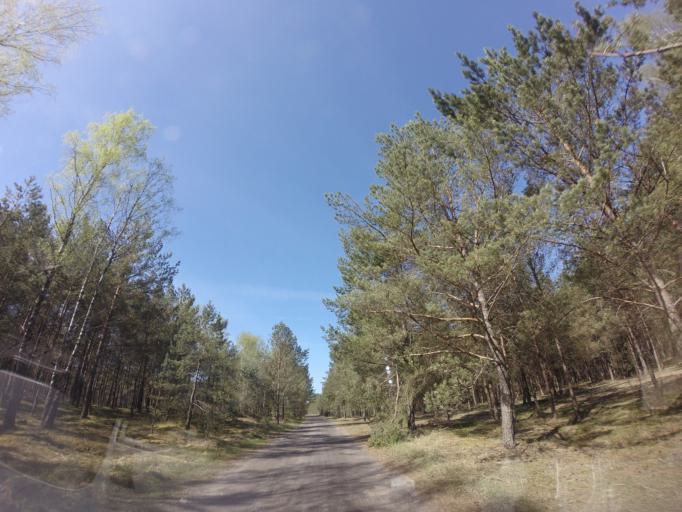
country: PL
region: West Pomeranian Voivodeship
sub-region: Powiat drawski
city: Kalisz Pomorski
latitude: 53.2071
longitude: 15.9564
